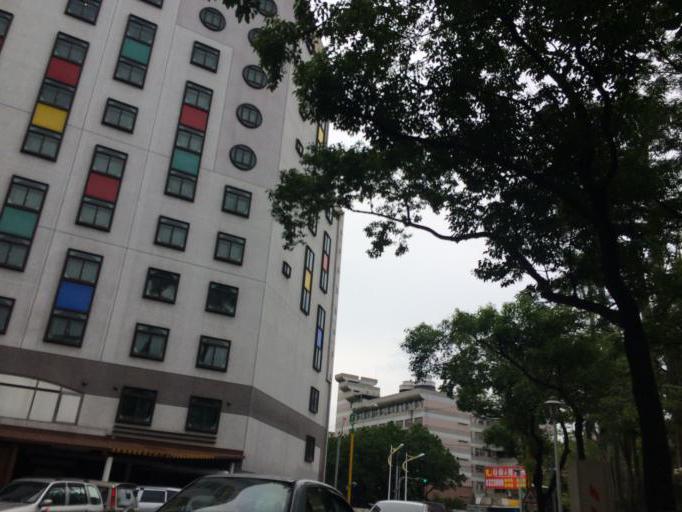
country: TW
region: Taiwan
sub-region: Hualien
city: Hualian
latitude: 23.9771
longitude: 121.6120
